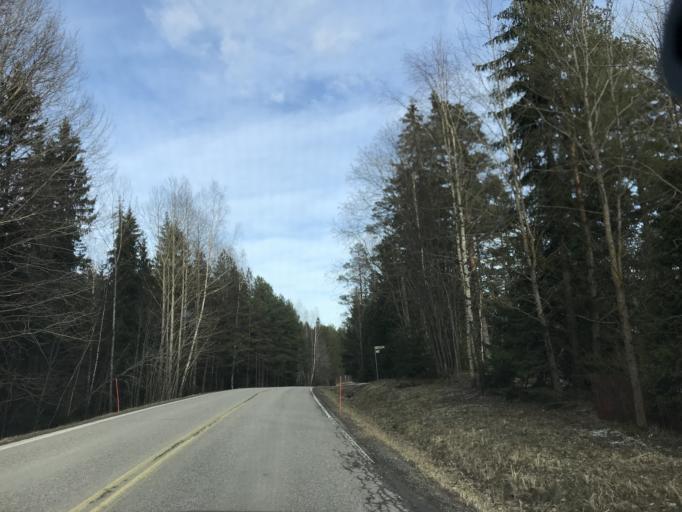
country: FI
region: Uusimaa
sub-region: Raaseporin
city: Pohja
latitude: 60.0916
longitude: 23.4602
